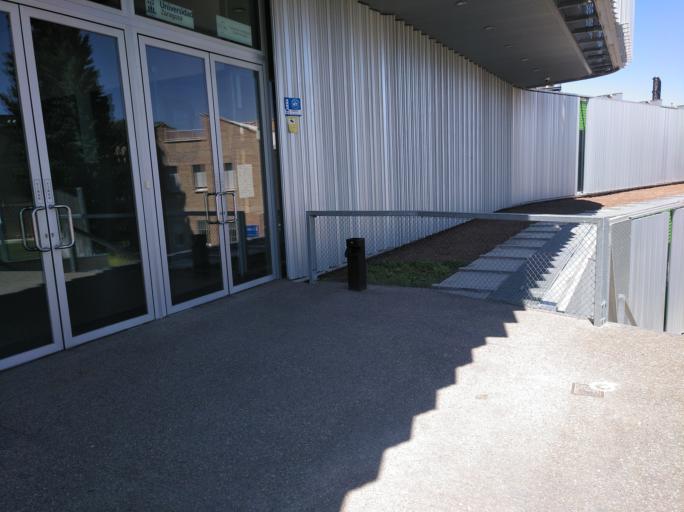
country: ES
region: Aragon
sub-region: Provincia de Zaragoza
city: Delicias
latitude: 41.6426
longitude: -0.9020
